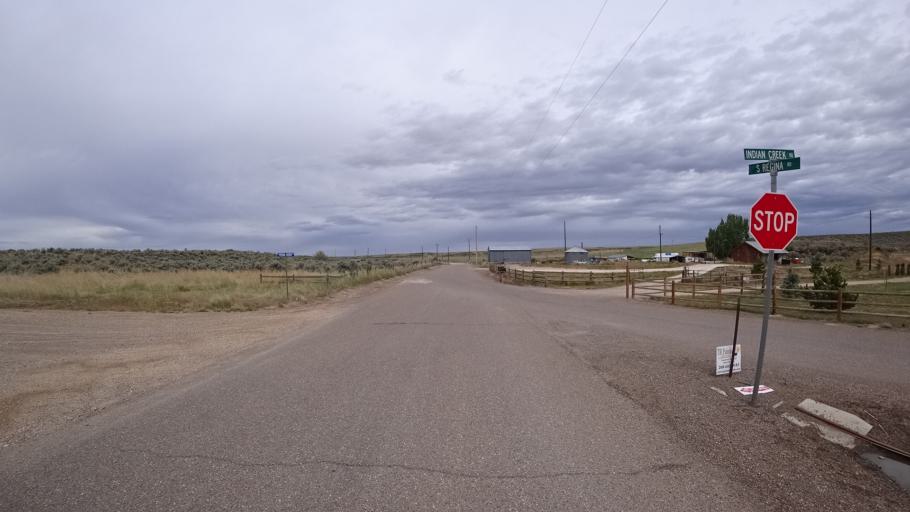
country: US
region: Idaho
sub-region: Ada County
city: Boise
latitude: 43.3884
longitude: -115.9729
